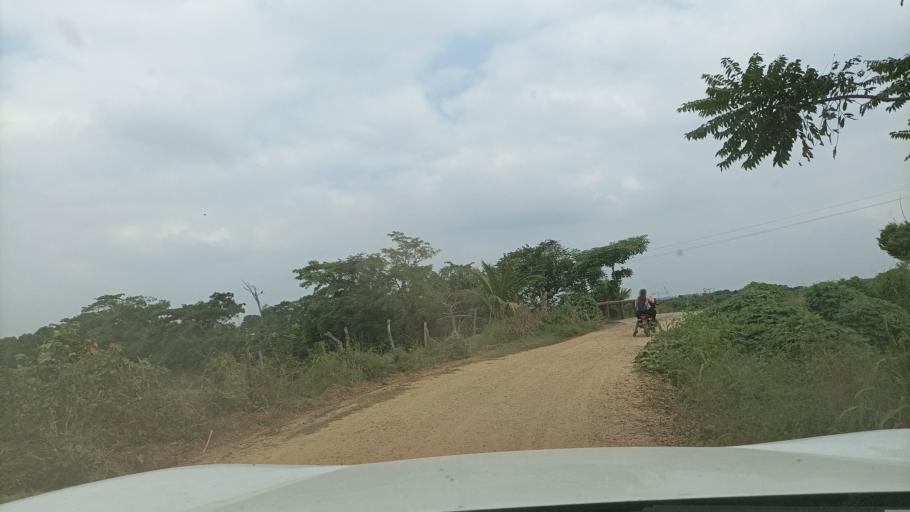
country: MX
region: Veracruz
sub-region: Texistepec
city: San Lorenzo Tenochtitlan
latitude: 17.7843
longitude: -94.7862
